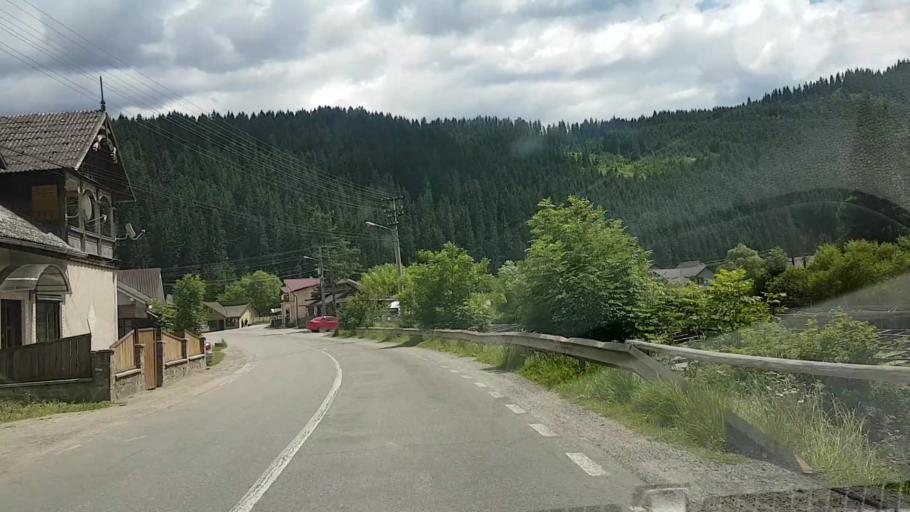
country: RO
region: Suceava
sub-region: Comuna Brosteni
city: Brosteni
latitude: 47.2379
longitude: 25.6943
